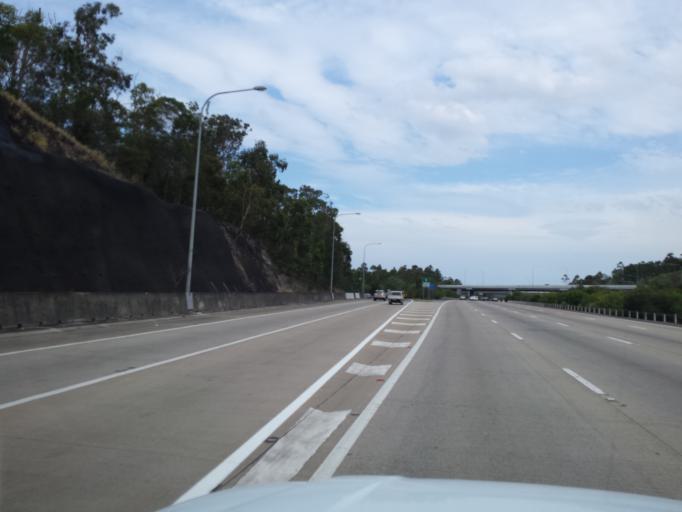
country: AU
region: Queensland
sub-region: Gold Coast
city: Upper Coomera
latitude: -27.9235
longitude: 153.3270
